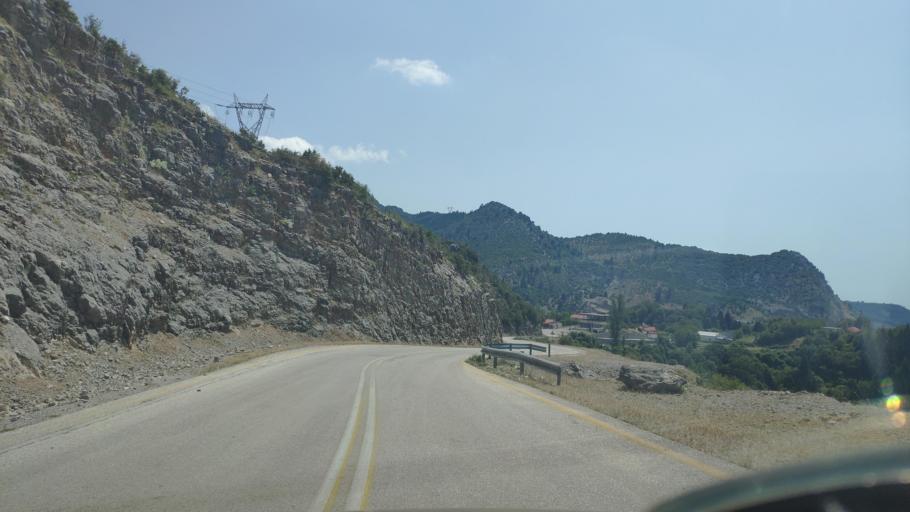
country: GR
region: Epirus
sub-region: Nomos Artas
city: Ano Kalentini
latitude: 39.2586
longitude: 21.2481
